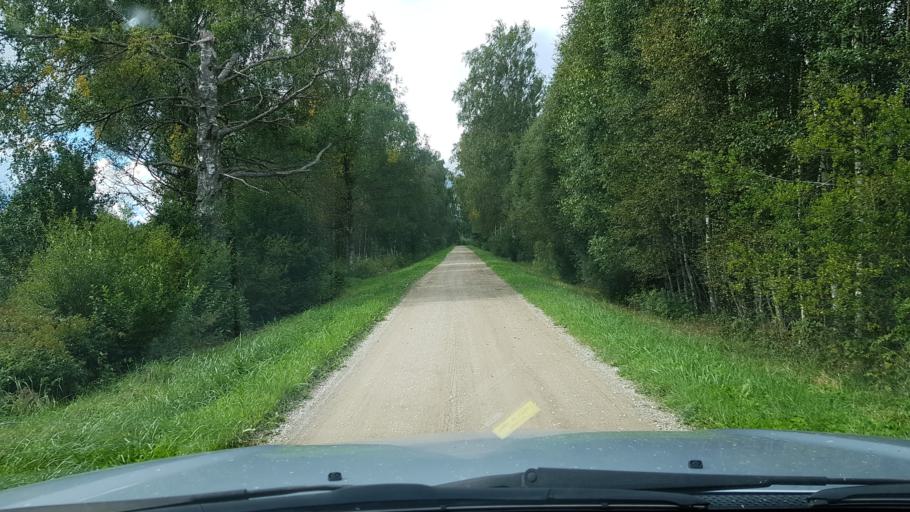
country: EE
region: Harju
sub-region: Raasiku vald
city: Arukula
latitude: 59.3034
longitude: 25.0679
